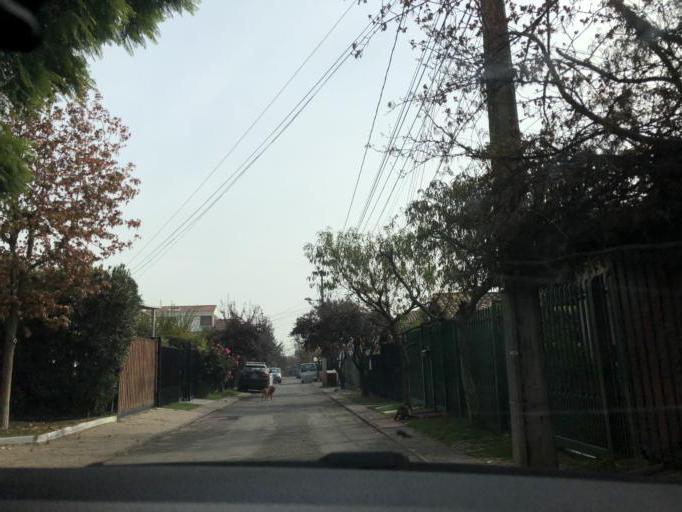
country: CL
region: Santiago Metropolitan
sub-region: Provincia de Cordillera
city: Puente Alto
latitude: -33.5493
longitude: -70.5614
